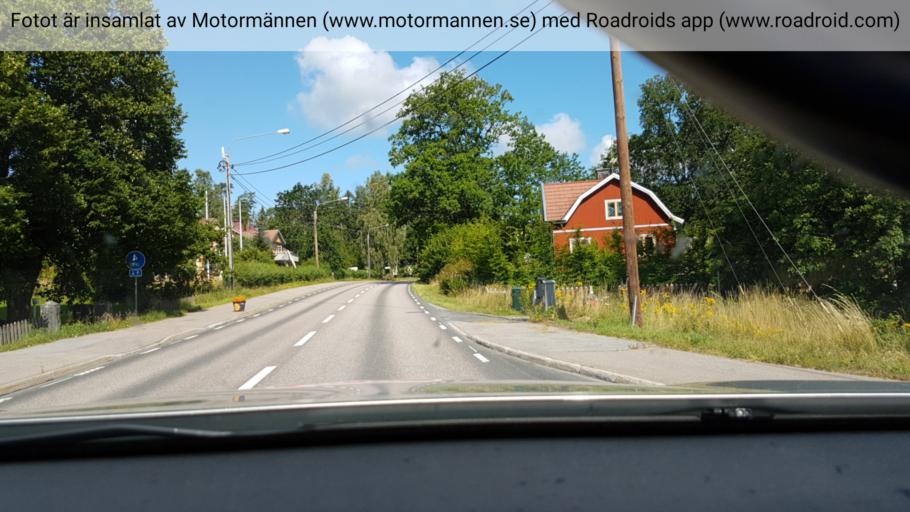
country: SE
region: Stockholm
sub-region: Norrtalje Kommun
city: Norrtalje
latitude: 59.8997
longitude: 18.7038
